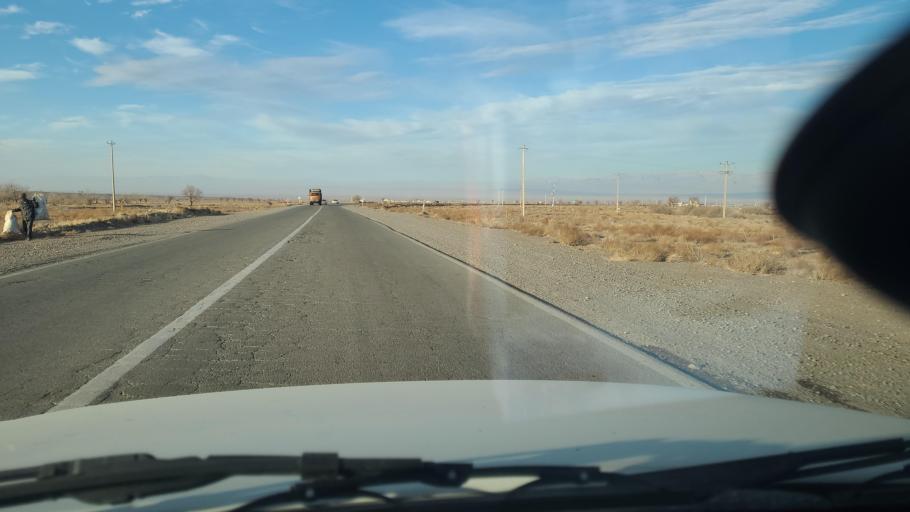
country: IR
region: Razavi Khorasan
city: Neqab
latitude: 36.4957
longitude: 57.5314
